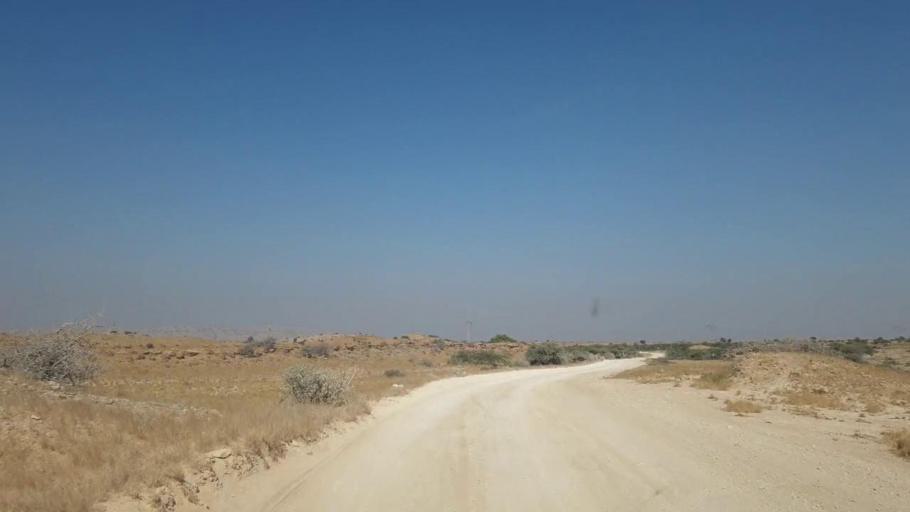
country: PK
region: Sindh
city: Thatta
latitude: 25.2364
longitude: 67.8041
